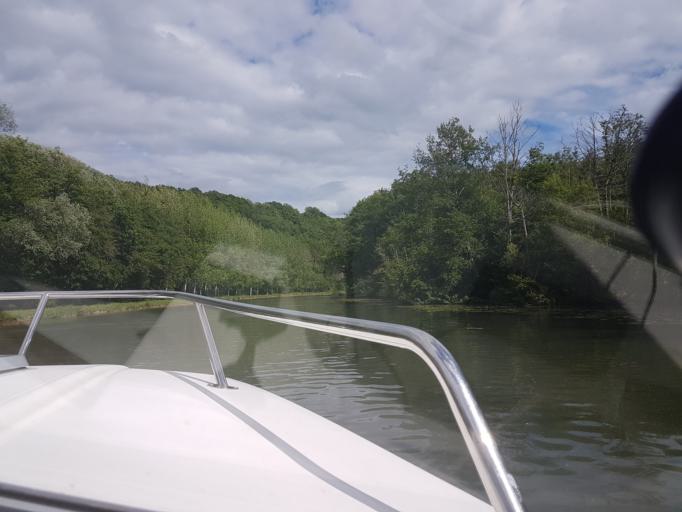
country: FR
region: Bourgogne
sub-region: Departement de l'Yonne
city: Vermenton
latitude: 47.5651
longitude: 3.6488
